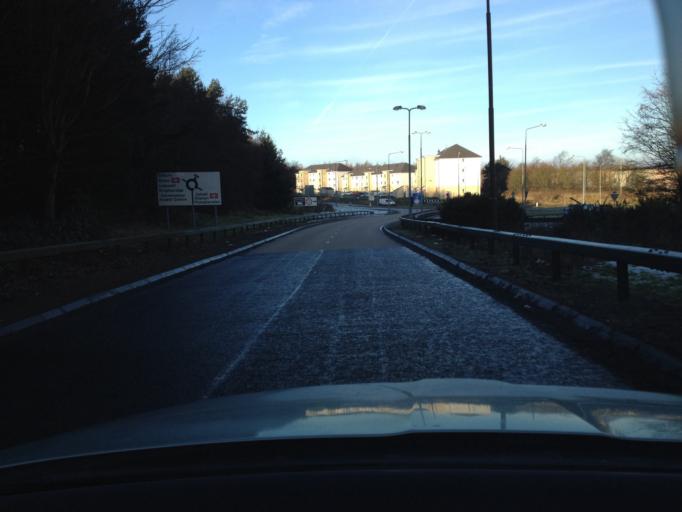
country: GB
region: Scotland
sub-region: West Lothian
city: Livingston
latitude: 55.9043
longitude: -3.5151
